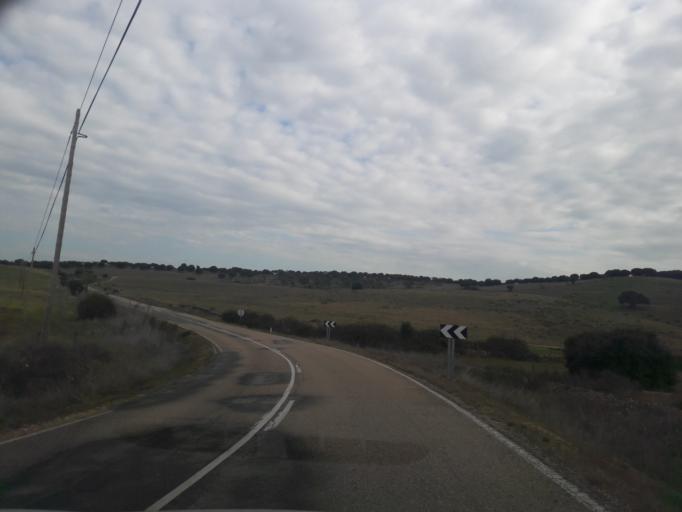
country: ES
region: Castille and Leon
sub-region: Provincia de Salamanca
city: Pastores
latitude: 40.5504
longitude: -6.5275
